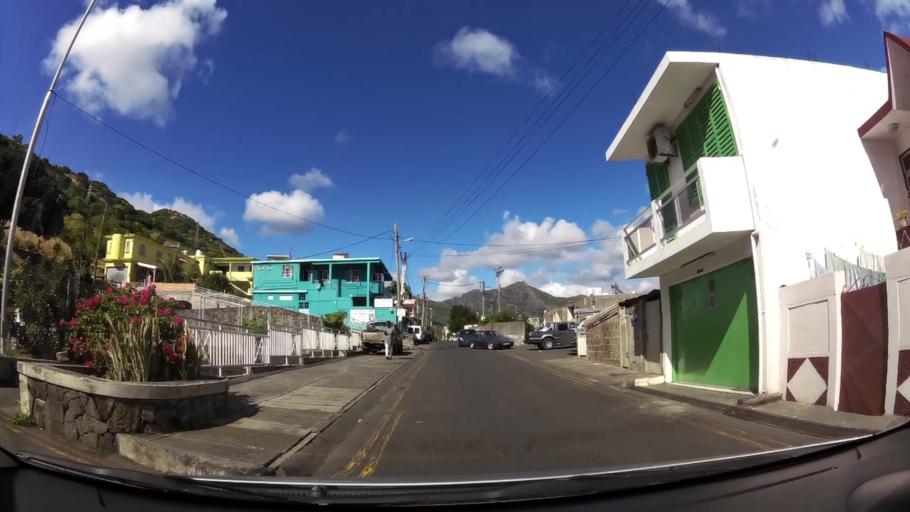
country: MU
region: Port Louis
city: Port Louis
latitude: -20.1564
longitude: 57.5196
